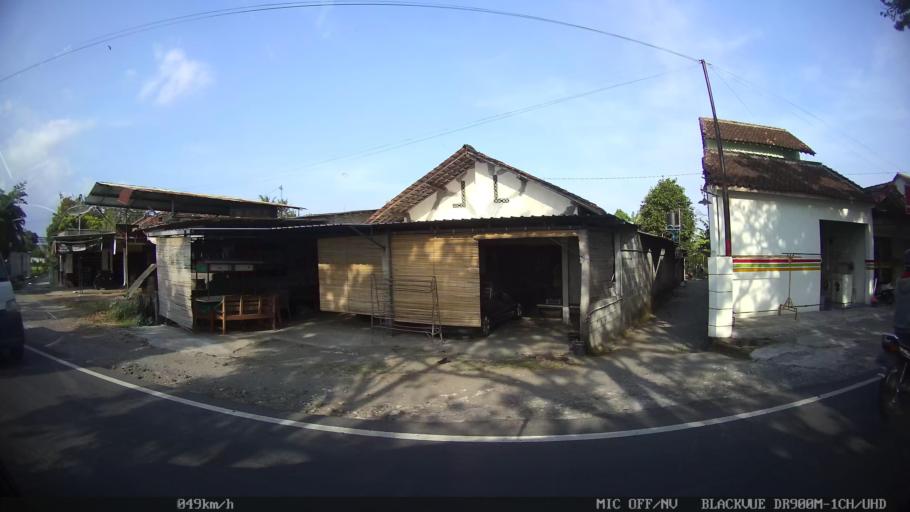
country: ID
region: Daerah Istimewa Yogyakarta
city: Bantul
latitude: -7.8800
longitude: 110.3196
